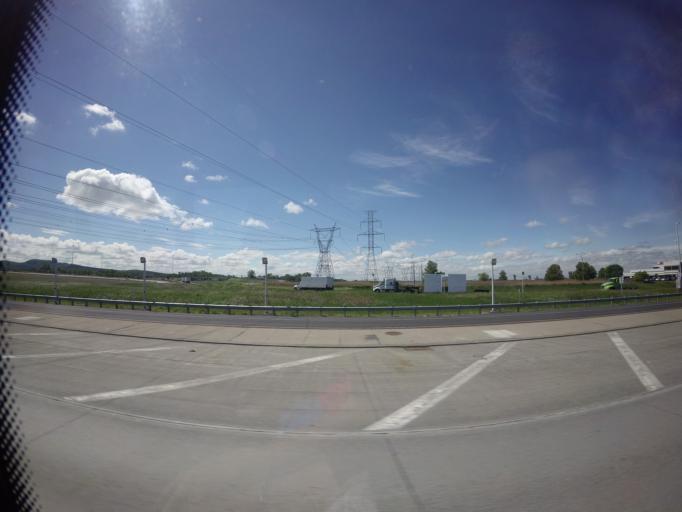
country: CA
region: Quebec
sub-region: Monteregie
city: Sainte-Julie
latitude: 45.5732
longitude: -73.3757
